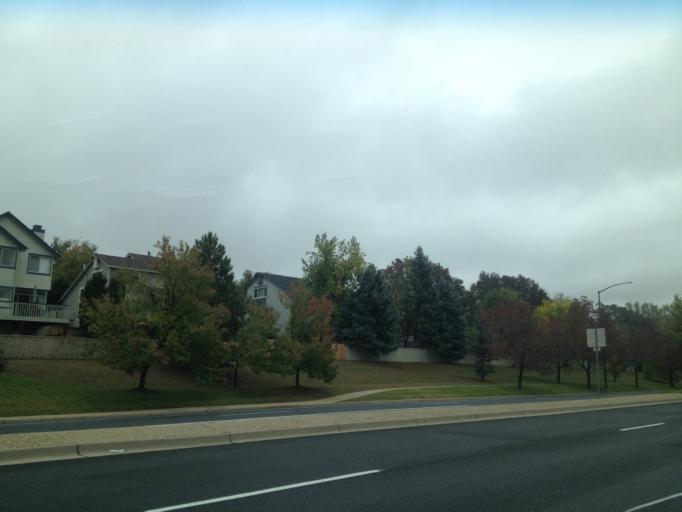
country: US
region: Colorado
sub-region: Boulder County
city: Louisville
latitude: 39.9767
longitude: -105.1537
